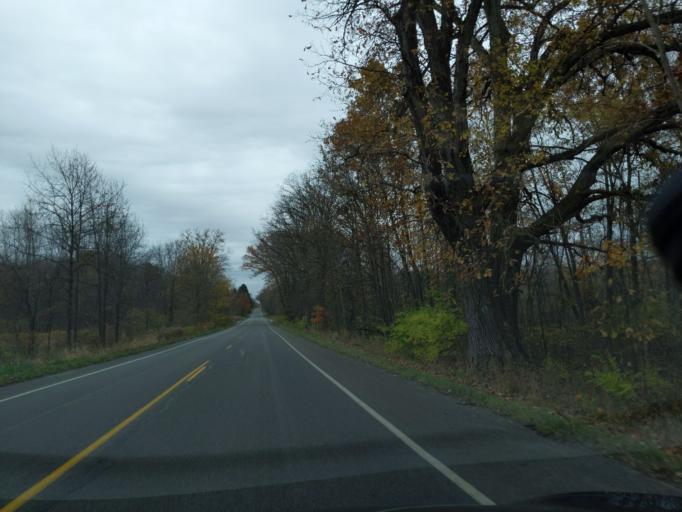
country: US
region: Michigan
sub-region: Jackson County
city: Spring Arbor
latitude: 42.2766
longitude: -84.5325
